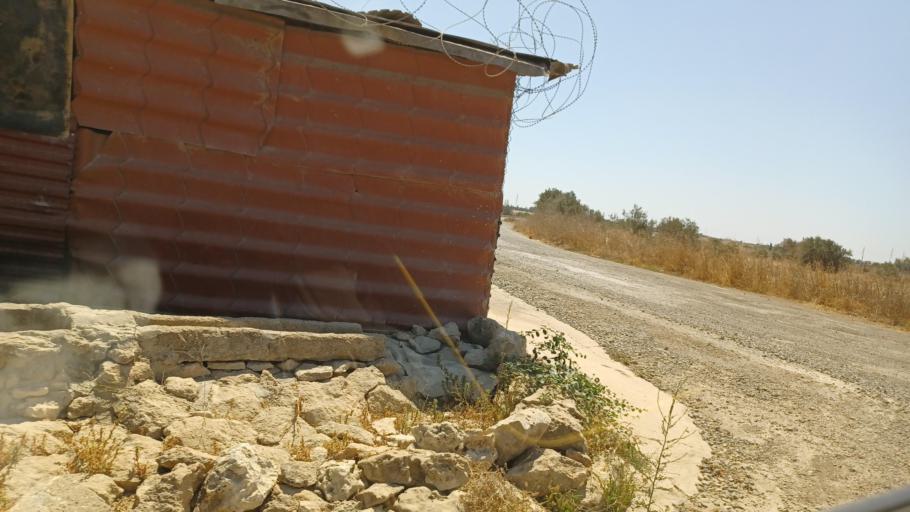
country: CY
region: Ammochostos
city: Acheritou
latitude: 35.0722
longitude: 33.8902
